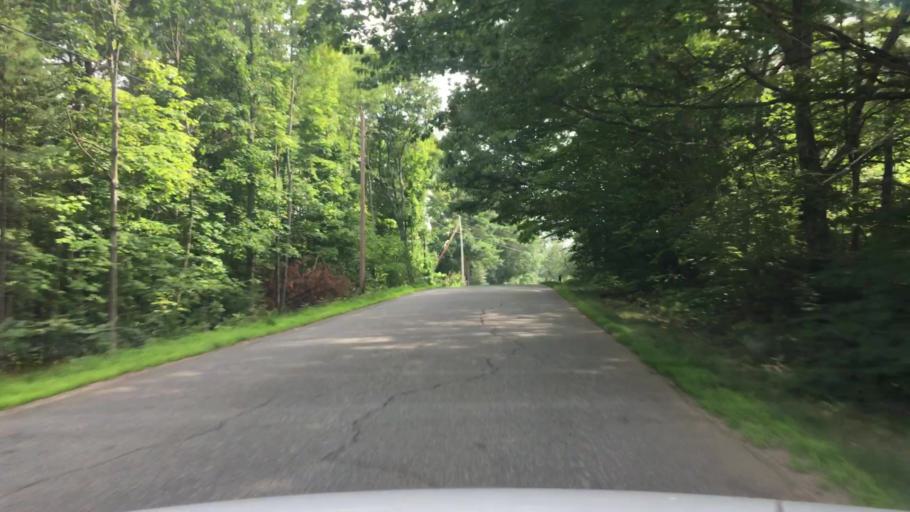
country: US
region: Maine
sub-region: Lincoln County
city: Jefferson
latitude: 44.2278
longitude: -69.4454
